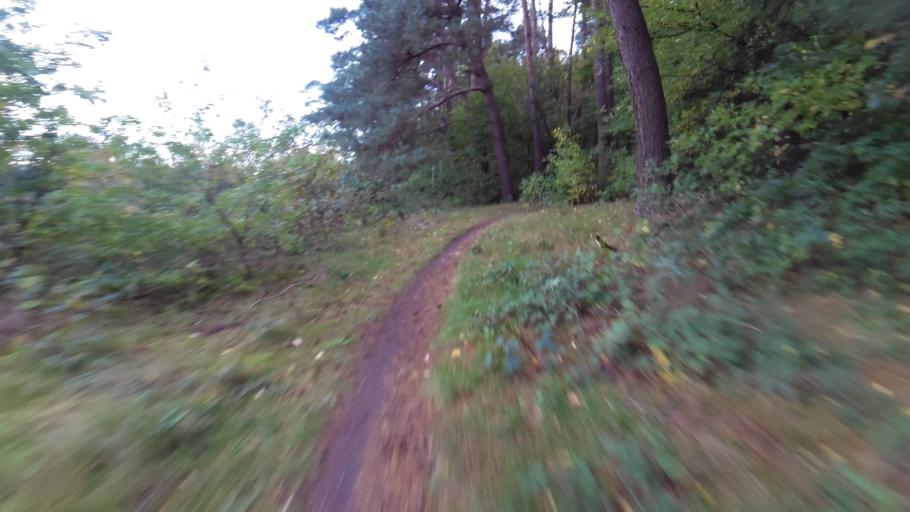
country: NL
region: Gelderland
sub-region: Gemeente Renkum
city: Oosterbeek
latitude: 52.0028
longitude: 5.8275
